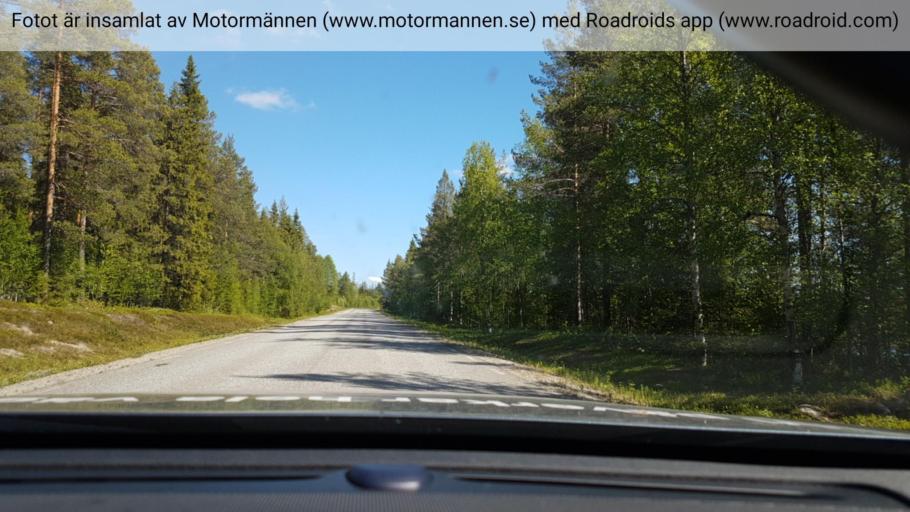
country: SE
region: Vaesterbotten
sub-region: Lycksele Kommun
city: Soderfors
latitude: 64.6319
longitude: 18.0280
